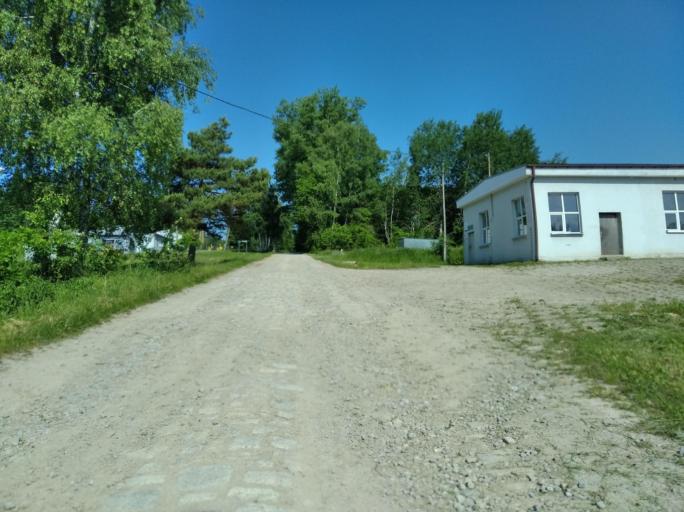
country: PL
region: Subcarpathian Voivodeship
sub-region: Powiat krosnienski
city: Odrzykon
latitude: 49.7720
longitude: 21.7642
